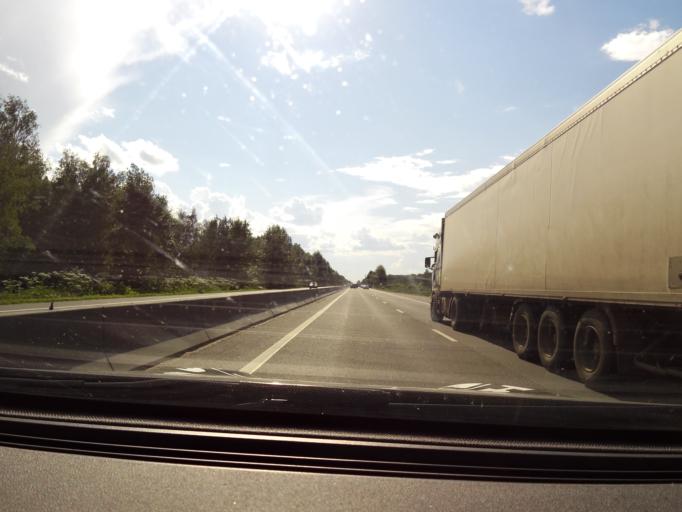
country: RU
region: Nizjnij Novgorod
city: Gorbatovka
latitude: 56.3104
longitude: 43.7869
